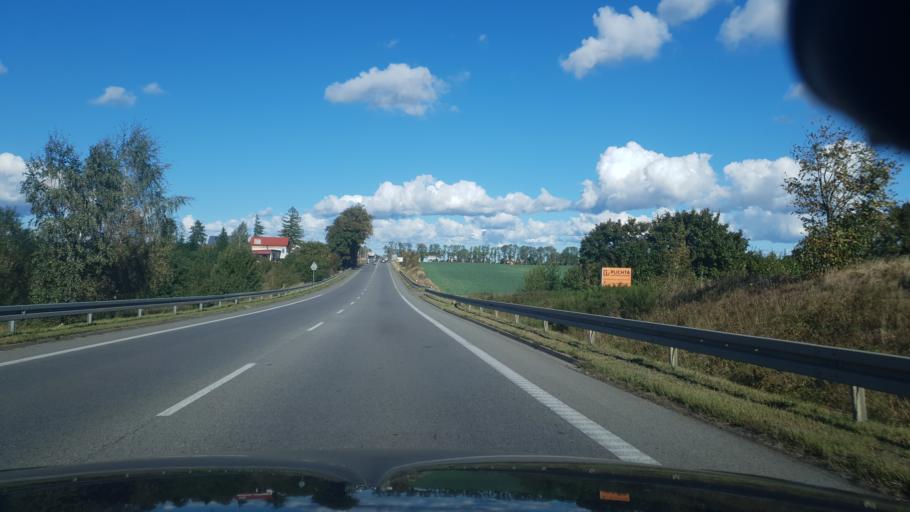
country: PL
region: Pomeranian Voivodeship
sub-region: Powiat pucki
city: Zelistrzewo
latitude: 54.6768
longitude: 18.3750
